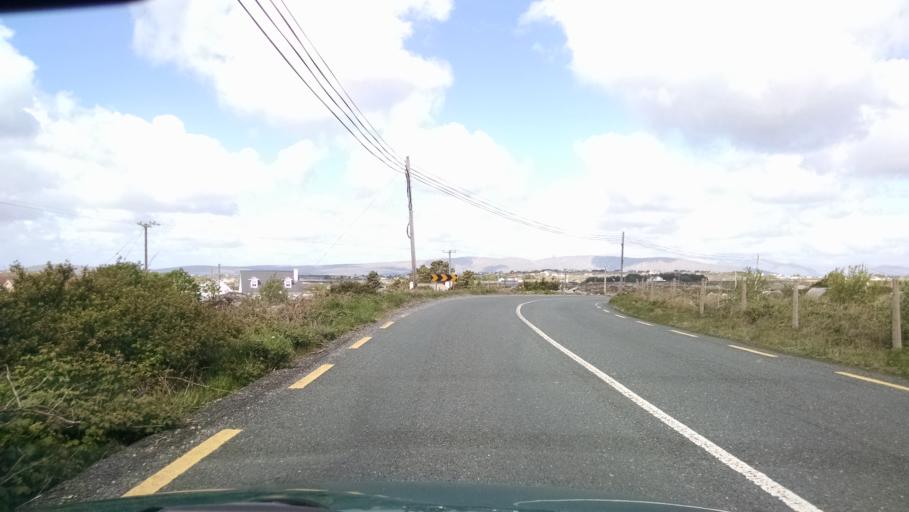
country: IE
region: Connaught
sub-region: County Galway
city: Oughterard
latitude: 53.3071
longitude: -9.5970
